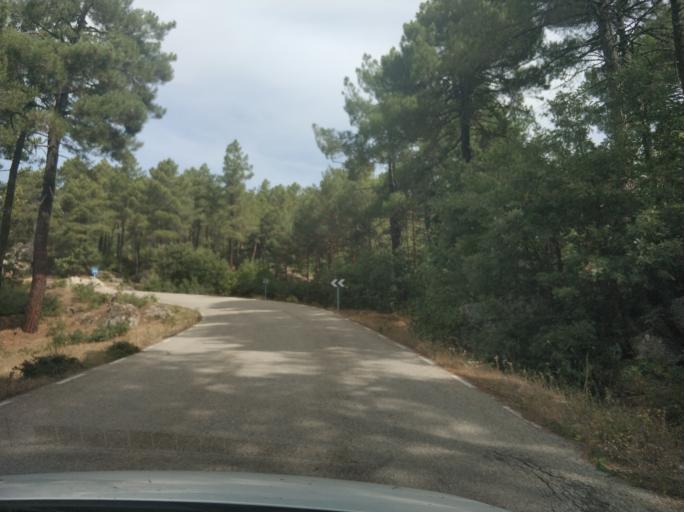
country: ES
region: Castille and Leon
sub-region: Provincia de Soria
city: Duruelo de la Sierra
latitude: 41.8938
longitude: -2.9452
